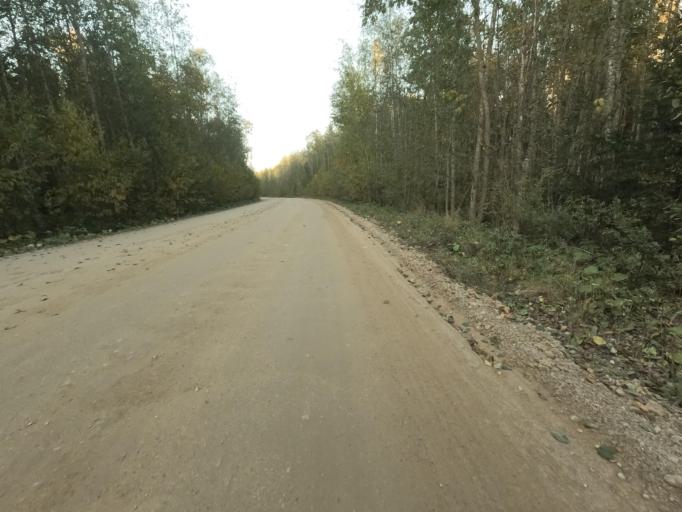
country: RU
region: Leningrad
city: Lyuban'
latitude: 58.9931
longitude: 31.1057
